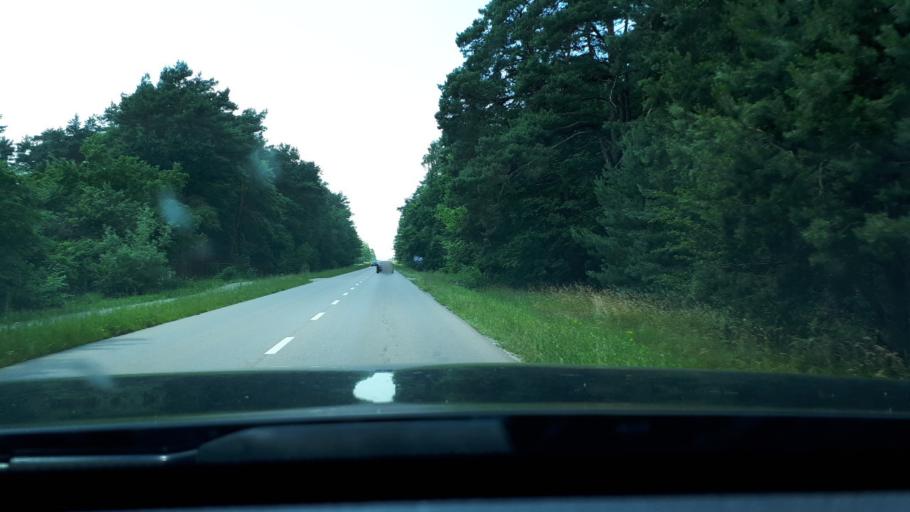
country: PL
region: Podlasie
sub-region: Powiat bialostocki
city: Choroszcz
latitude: 53.1311
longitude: 23.0394
